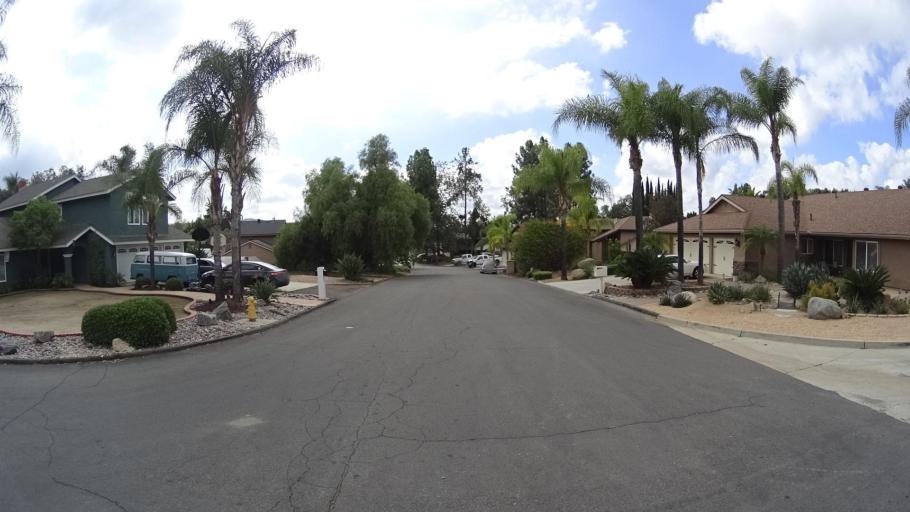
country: US
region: California
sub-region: San Diego County
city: Rancho San Diego
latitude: 32.7685
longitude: -116.9167
